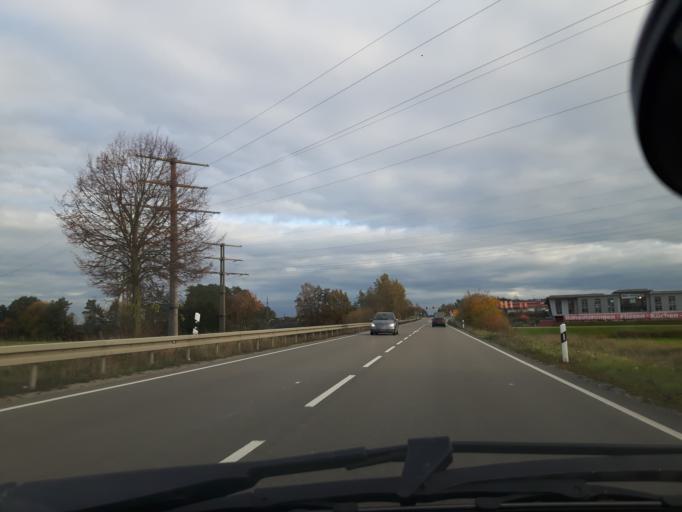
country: DE
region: Bavaria
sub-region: Regierungsbezirk Mittelfranken
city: Burgoberbach
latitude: 49.2446
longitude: 10.6019
